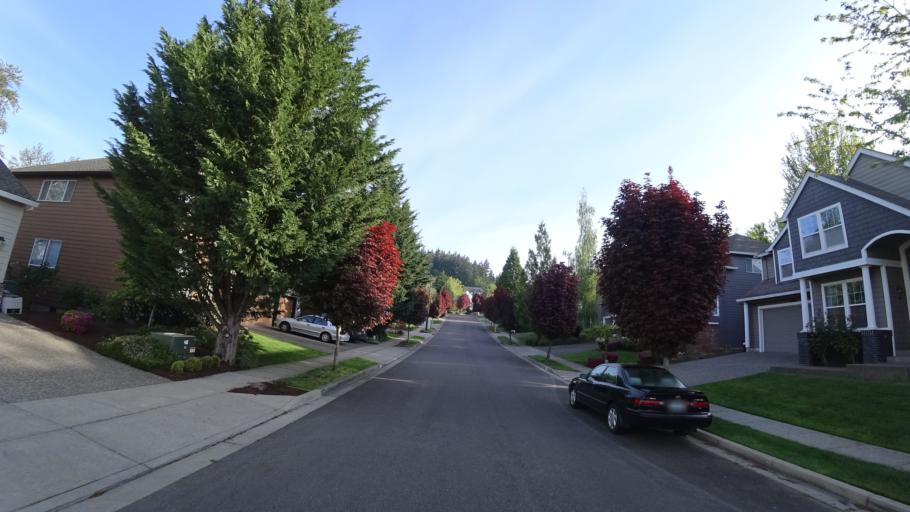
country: US
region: Oregon
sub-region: Washington County
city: King City
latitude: 45.4319
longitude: -122.8461
